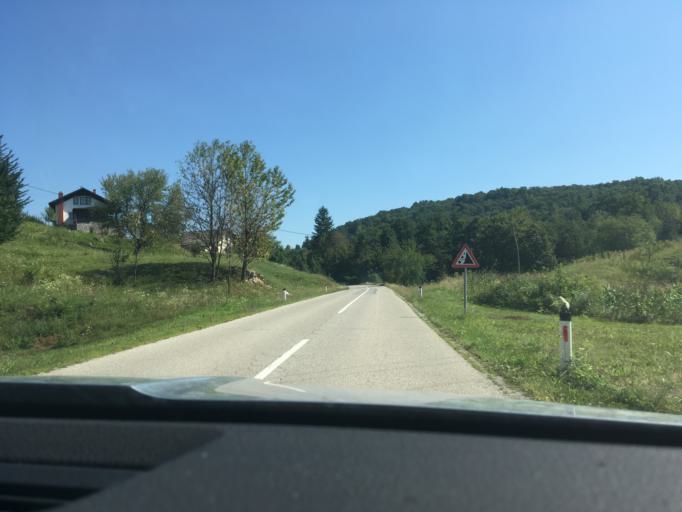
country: SI
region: Metlika
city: Metlika
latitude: 45.5251
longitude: 15.3077
